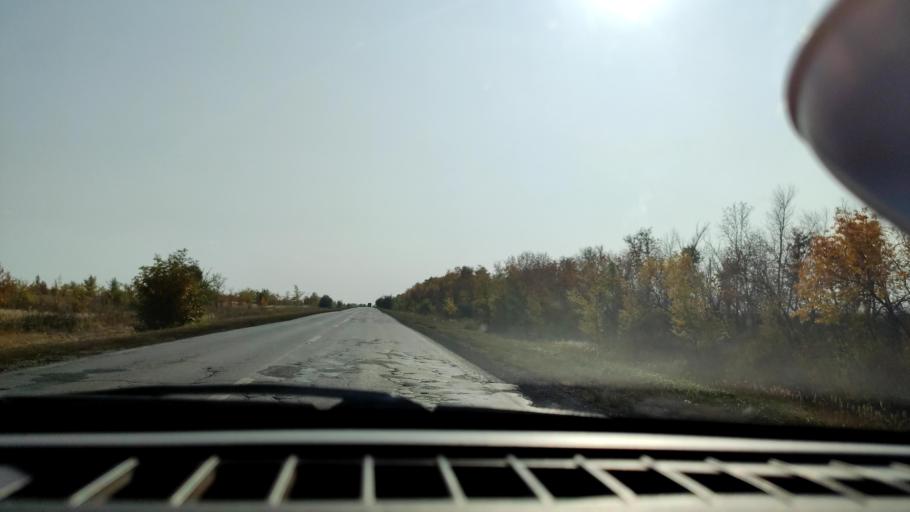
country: RU
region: Samara
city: Smyshlyayevka
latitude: 53.1284
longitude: 50.3696
